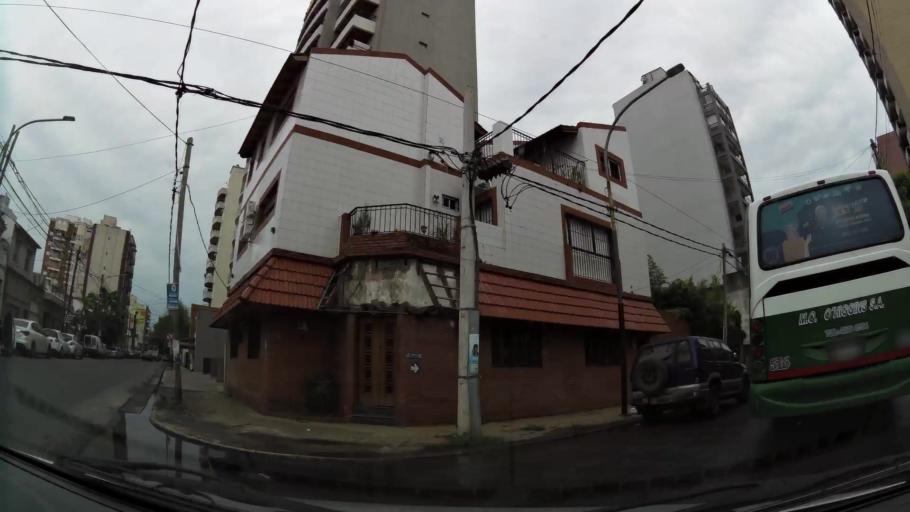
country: AR
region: Buenos Aires
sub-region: Partido de Lanus
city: Lanus
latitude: -34.7120
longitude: -58.3883
